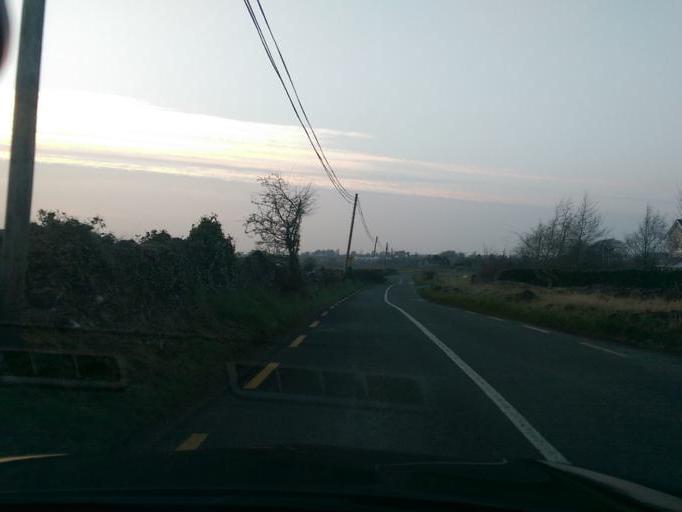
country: IE
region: Connaught
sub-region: County Galway
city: Loughrea
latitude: 53.2232
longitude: -8.6271
